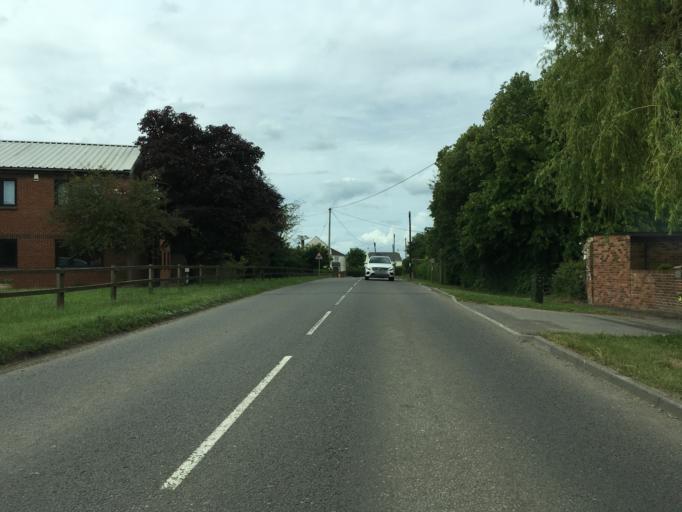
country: GB
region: England
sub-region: Wiltshire
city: Lyneham
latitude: 51.5600
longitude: -1.9891
